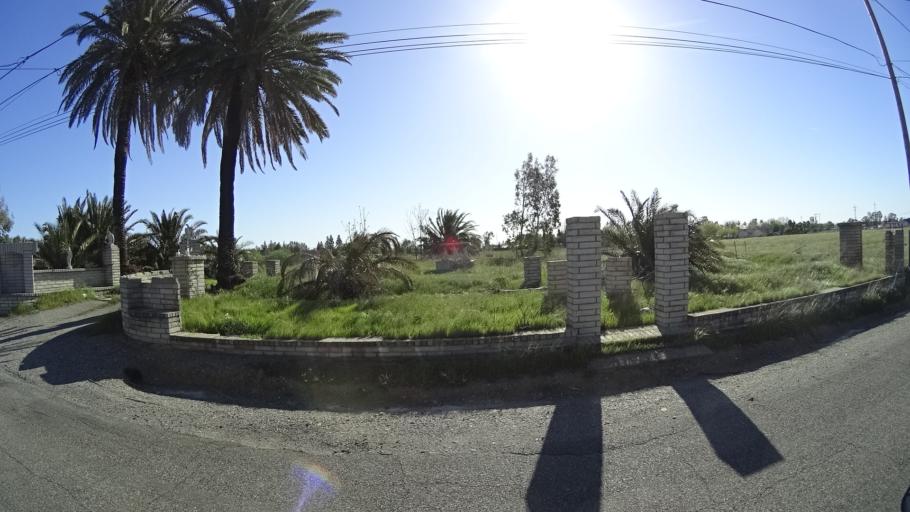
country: US
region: California
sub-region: Glenn County
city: Orland
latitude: 39.7577
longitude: -122.2200
